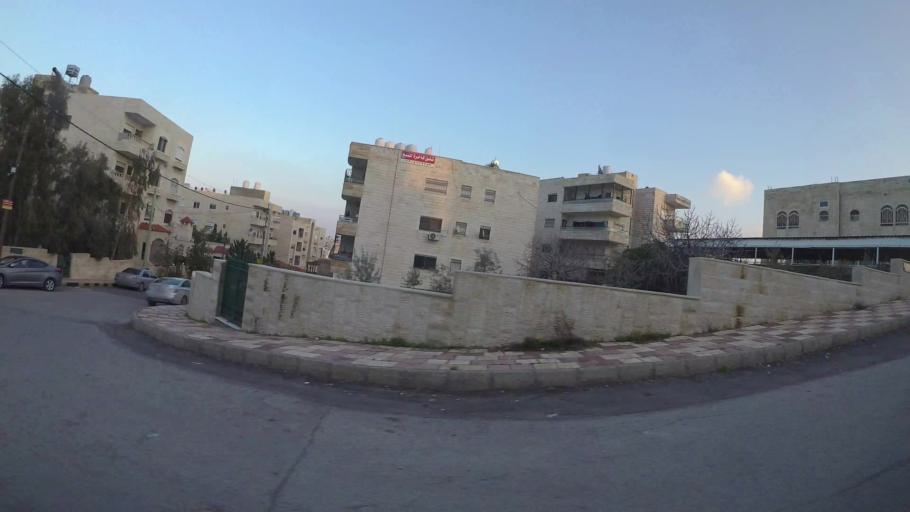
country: JO
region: Amman
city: Amman
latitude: 31.9928
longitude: 35.9523
